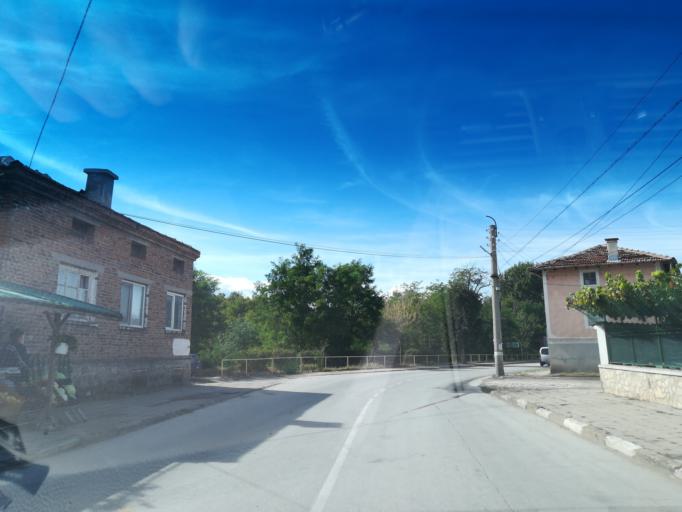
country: BG
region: Plovdiv
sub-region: Obshtina Krichim
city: Krichim
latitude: 42.0852
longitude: 24.4309
